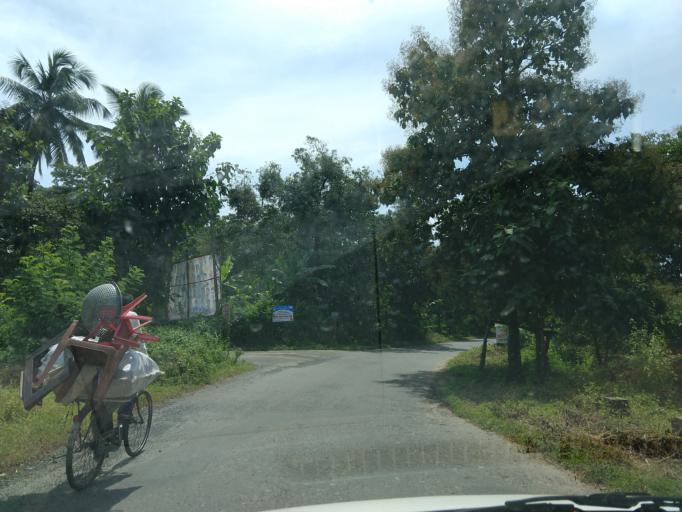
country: IN
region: Maharashtra
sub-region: Sindhudurg
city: Savantvadi
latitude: 15.9538
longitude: 73.7732
